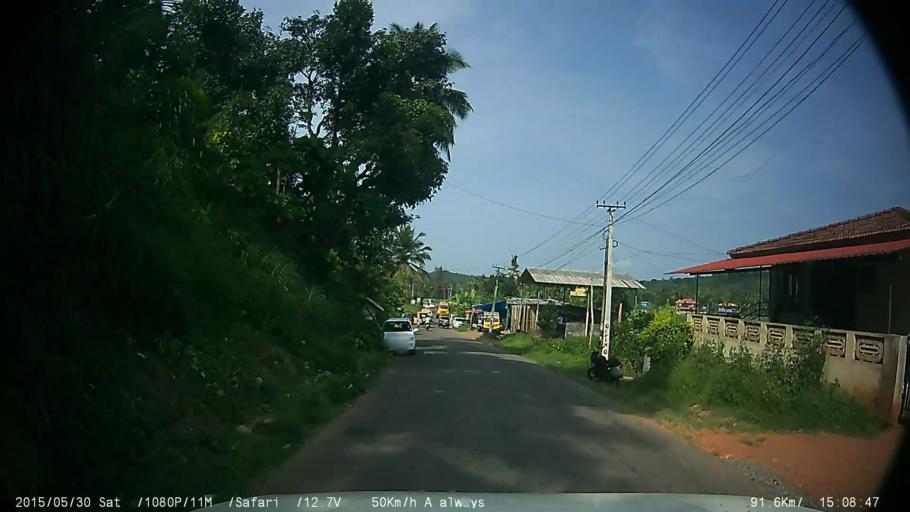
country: IN
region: Kerala
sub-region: Wayanad
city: Panamaram
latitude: 11.7983
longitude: 76.0229
